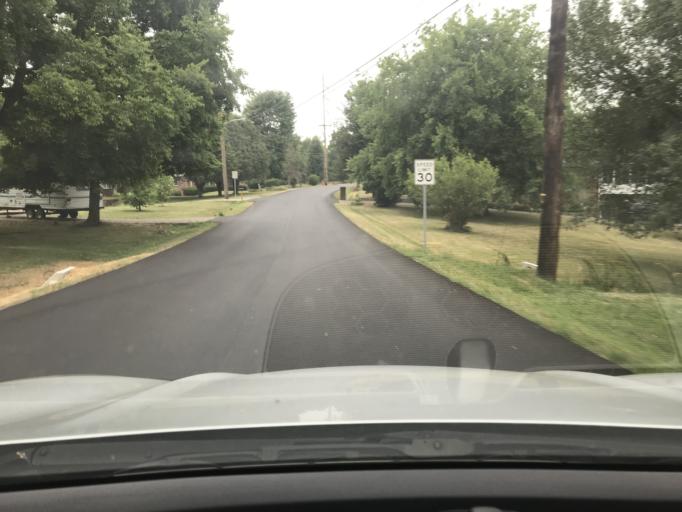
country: US
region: Tennessee
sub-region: Davidson County
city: Goodlettsville
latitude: 36.3012
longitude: -86.7147
